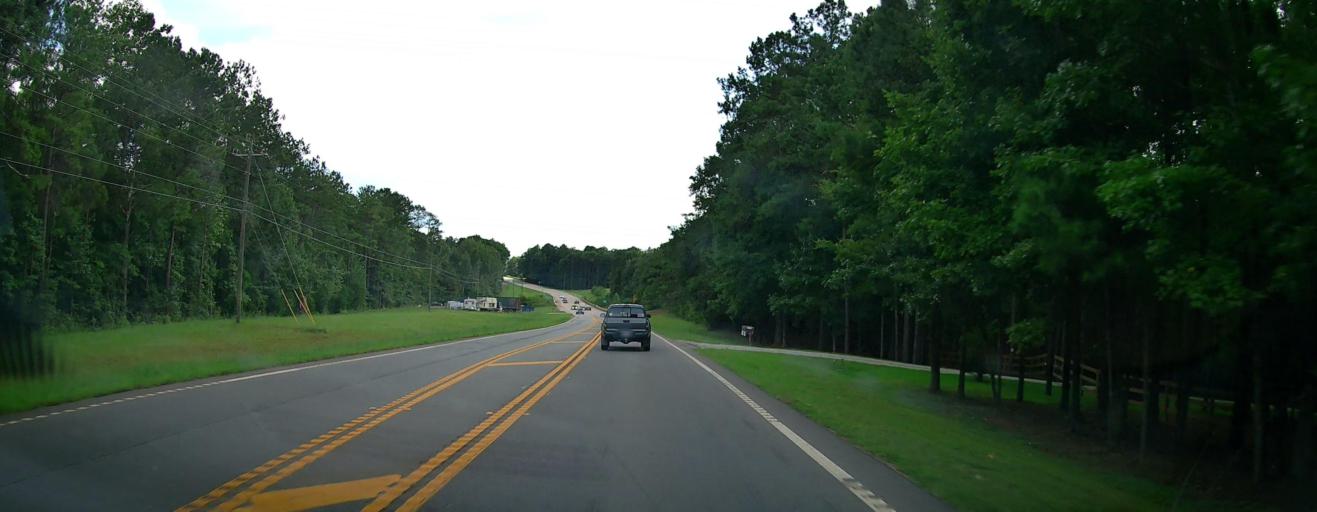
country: US
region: Georgia
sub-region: Harris County
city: Hamilton
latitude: 32.7111
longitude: -84.8716
